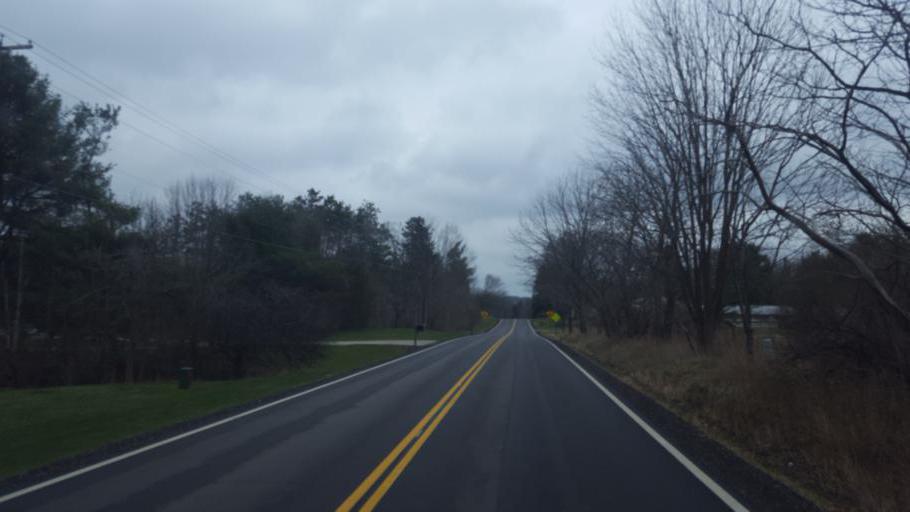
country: US
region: Ohio
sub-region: Medina County
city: Medina
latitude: 41.1065
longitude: -81.8132
